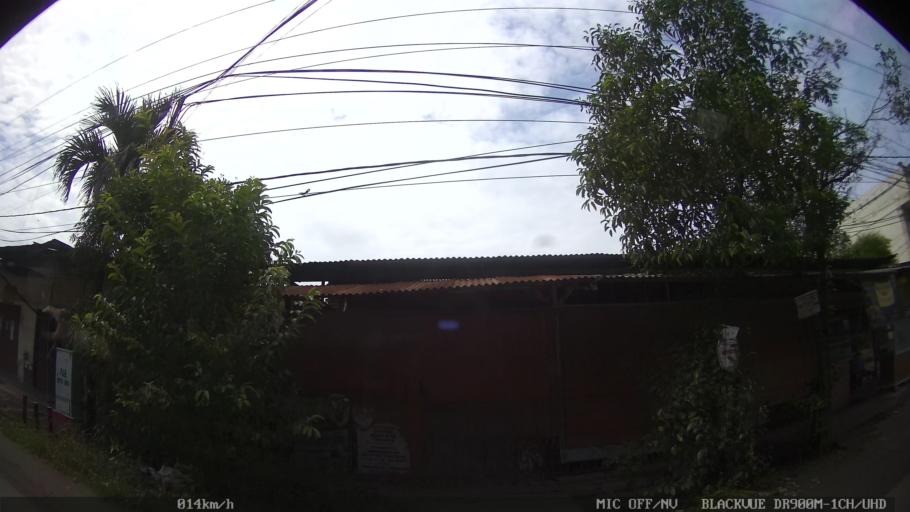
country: ID
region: North Sumatra
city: Medan
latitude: 3.5866
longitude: 98.7309
